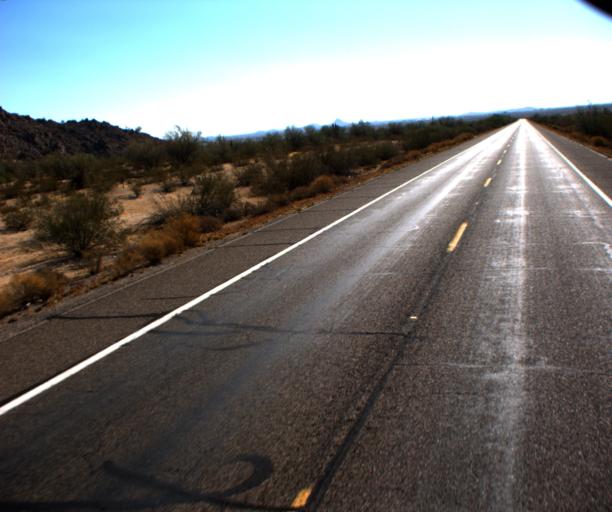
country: US
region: Arizona
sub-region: Pinal County
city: Blackwater
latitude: 33.0181
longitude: -111.6526
